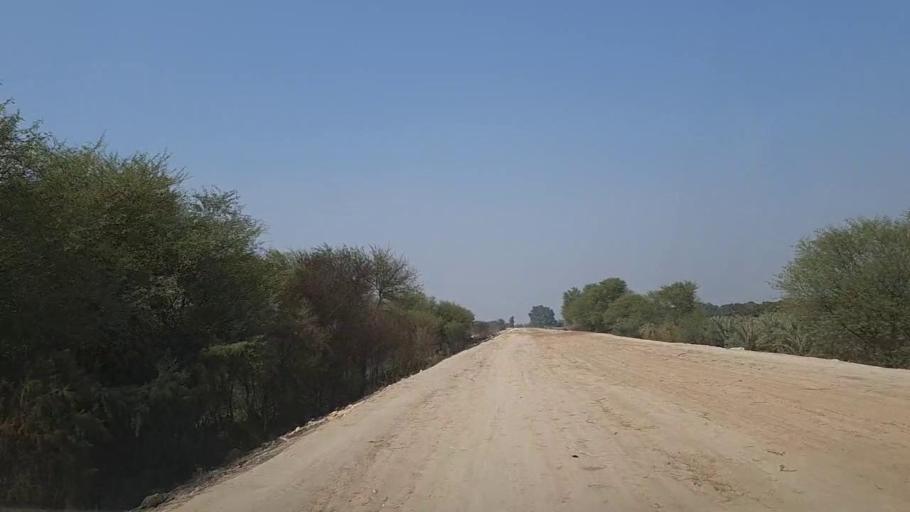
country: PK
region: Sindh
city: Moro
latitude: 26.8155
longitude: 67.9548
